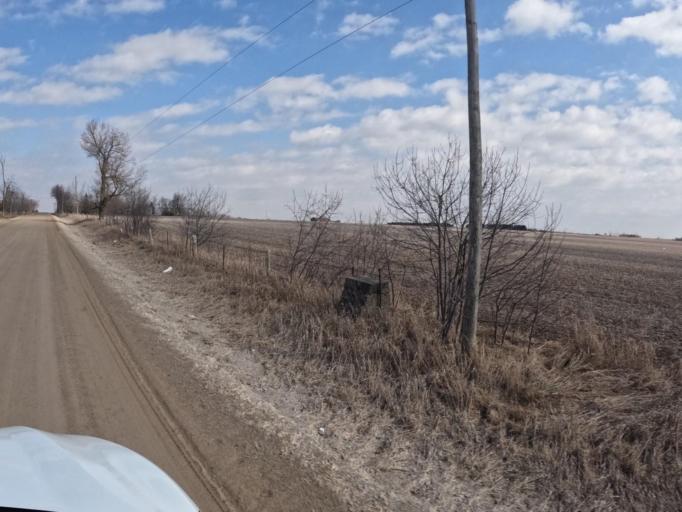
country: CA
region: Ontario
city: Orangeville
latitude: 43.9110
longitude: -80.2532
